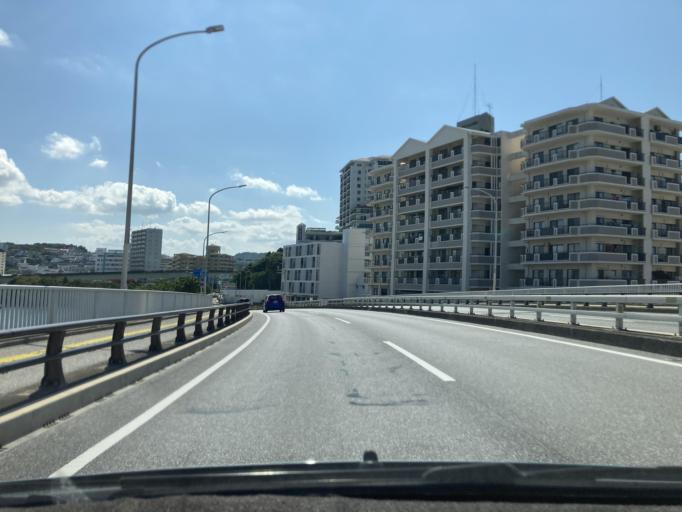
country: JP
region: Okinawa
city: Ginowan
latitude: 26.2702
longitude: 127.7259
